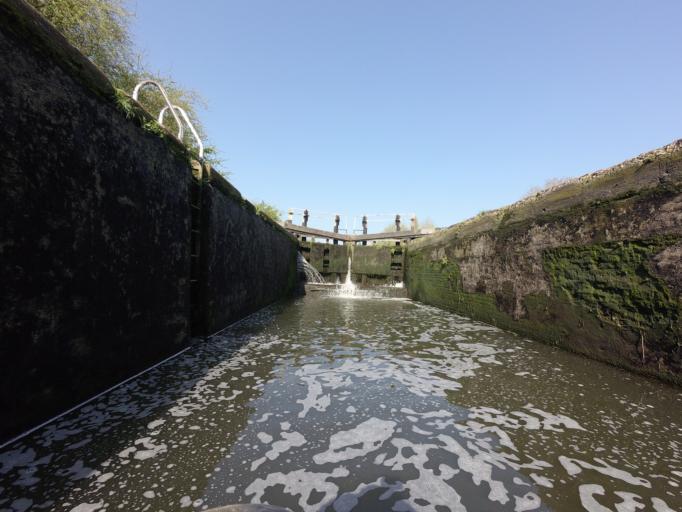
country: GB
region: England
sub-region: Hertfordshire
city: Bovingdon
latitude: 51.7473
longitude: -0.5235
